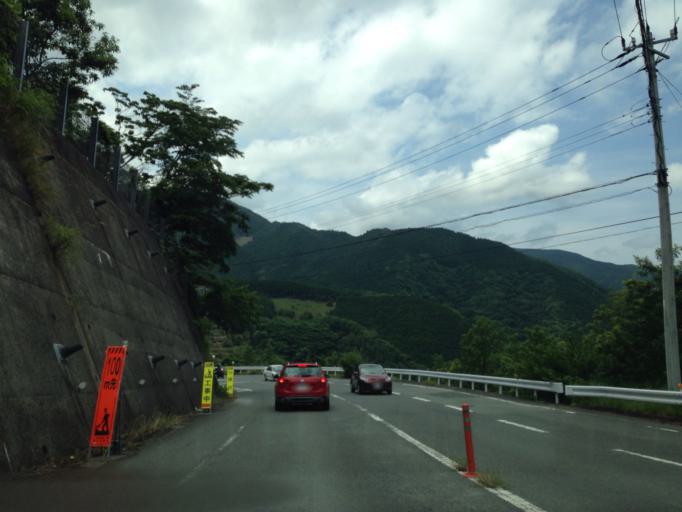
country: JP
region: Shizuoka
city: Heda
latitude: 34.9096
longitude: 138.8178
